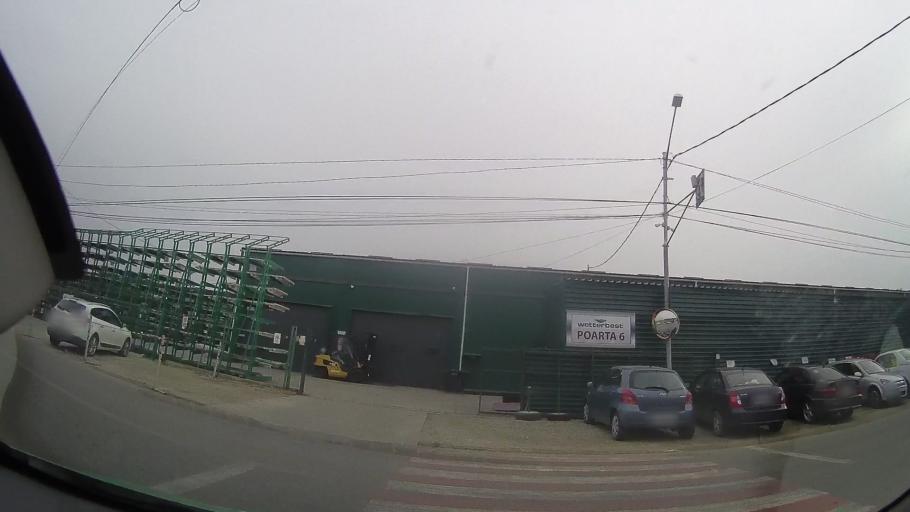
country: RO
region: Prahova
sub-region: Oras Baicoi
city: Liliesti
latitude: 45.0235
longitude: 25.8860
